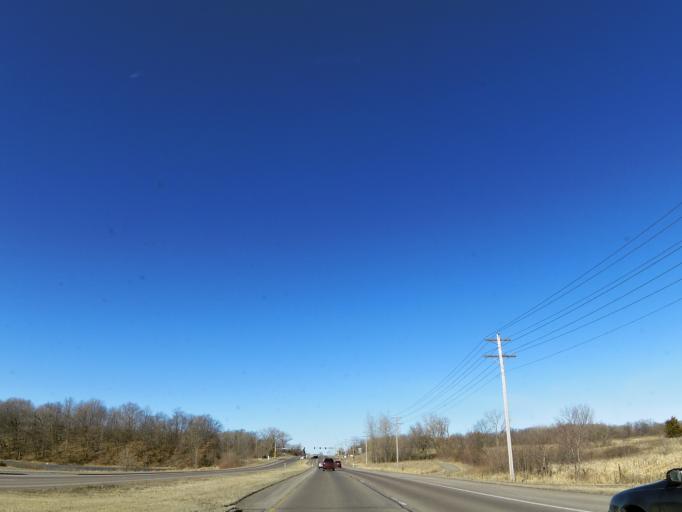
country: US
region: Minnesota
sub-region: Scott County
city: Prior Lake
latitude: 44.7470
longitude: -93.4461
